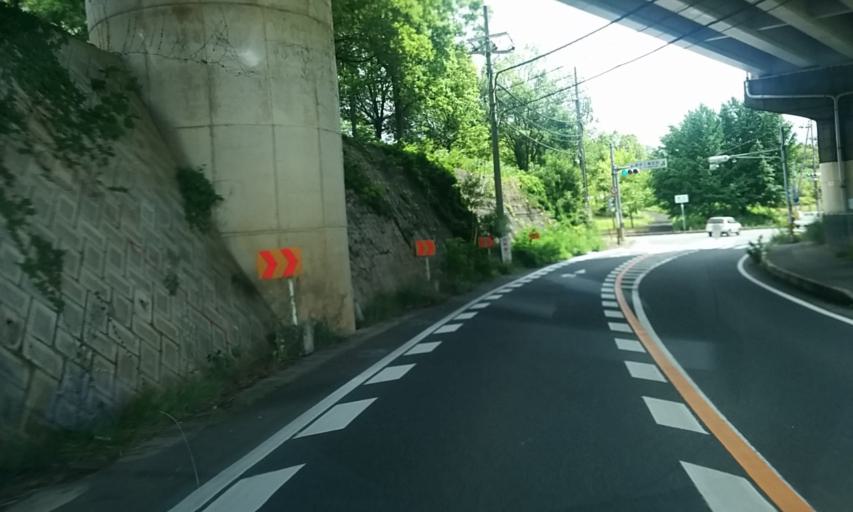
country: JP
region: Kyoto
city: Ayabe
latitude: 35.3303
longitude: 135.2679
